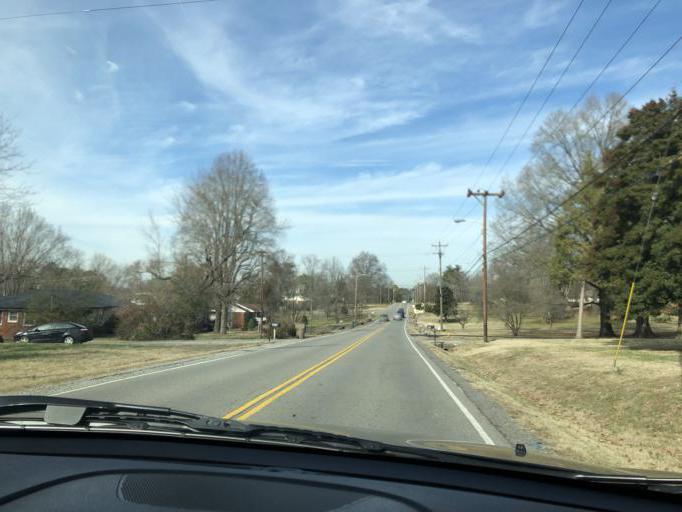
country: US
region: Tennessee
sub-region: Davidson County
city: Lakewood
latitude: 36.2015
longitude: -86.6772
